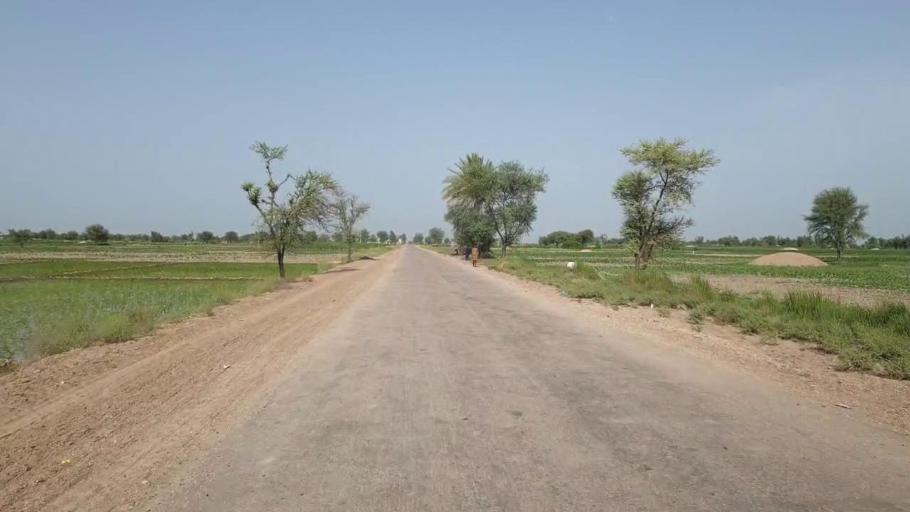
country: PK
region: Sindh
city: Sakrand
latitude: 26.2847
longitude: 68.2292
